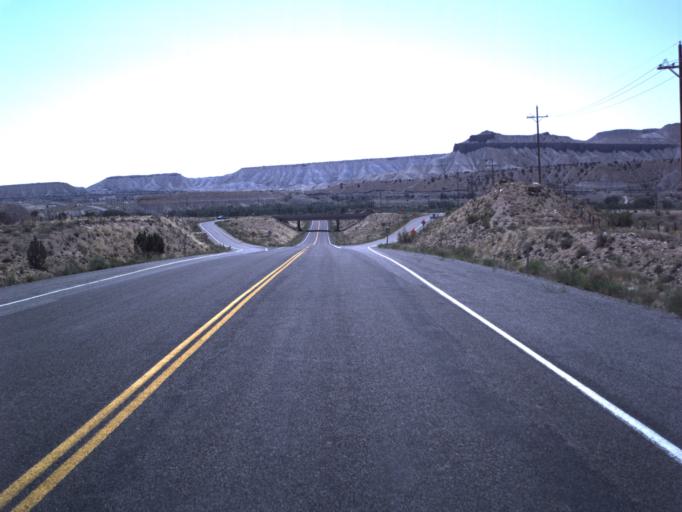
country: US
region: Utah
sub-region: Emery County
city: Orangeville
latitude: 39.2586
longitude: -111.0984
